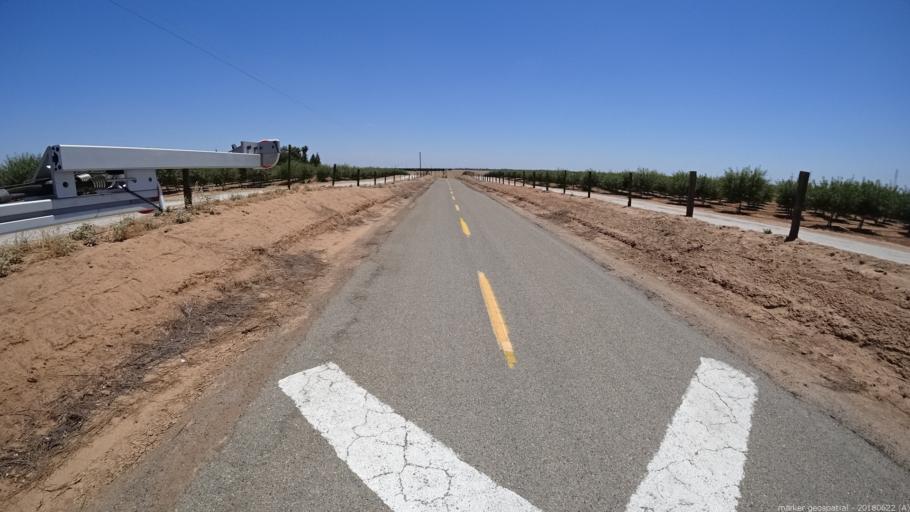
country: US
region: California
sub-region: Madera County
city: Bonadelle Ranchos-Madera Ranchos
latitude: 36.8661
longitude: -119.8317
